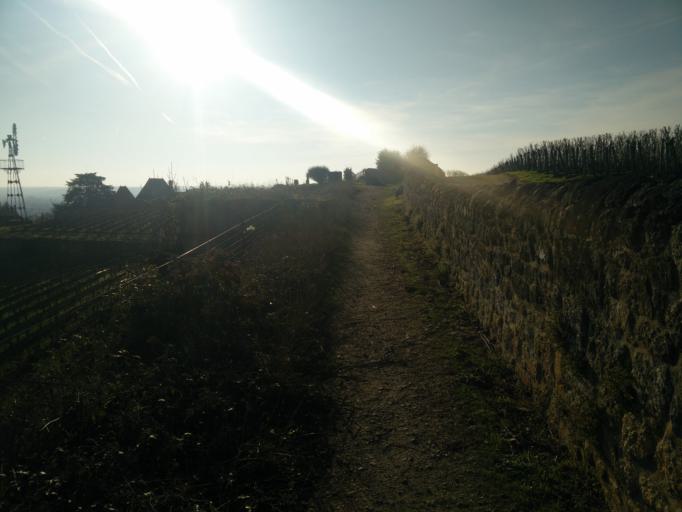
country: FR
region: Aquitaine
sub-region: Departement de la Gironde
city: Saint-Emilion
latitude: 44.8892
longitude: -0.1578
